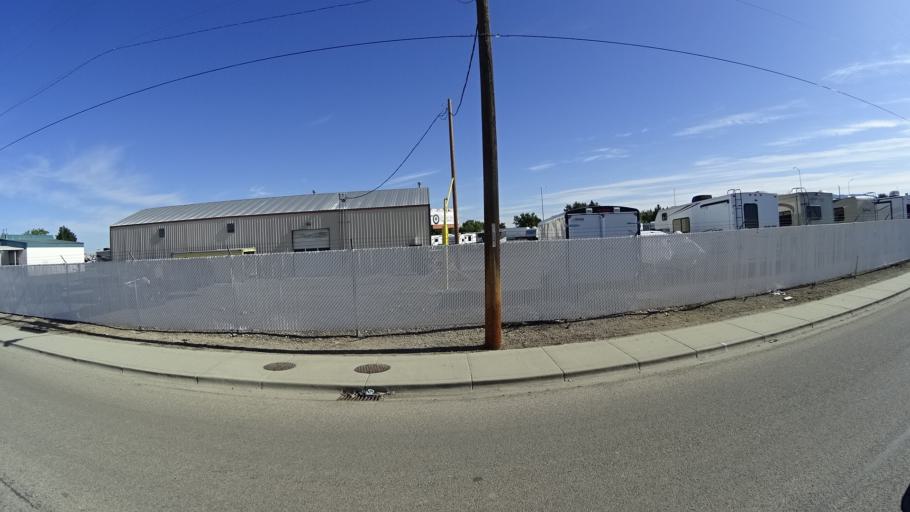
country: US
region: Idaho
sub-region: Ada County
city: Garden City
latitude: 43.5827
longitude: -116.2619
